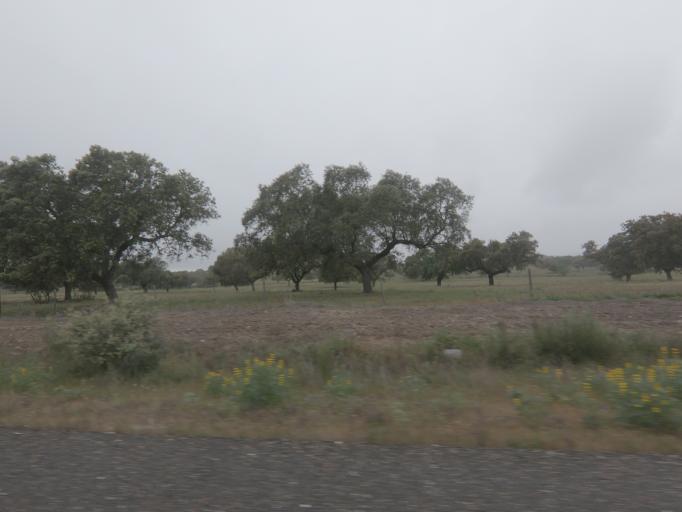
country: ES
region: Extremadura
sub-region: Provincia de Badajoz
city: La Roca de la Sierra
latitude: 39.0977
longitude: -6.7129
